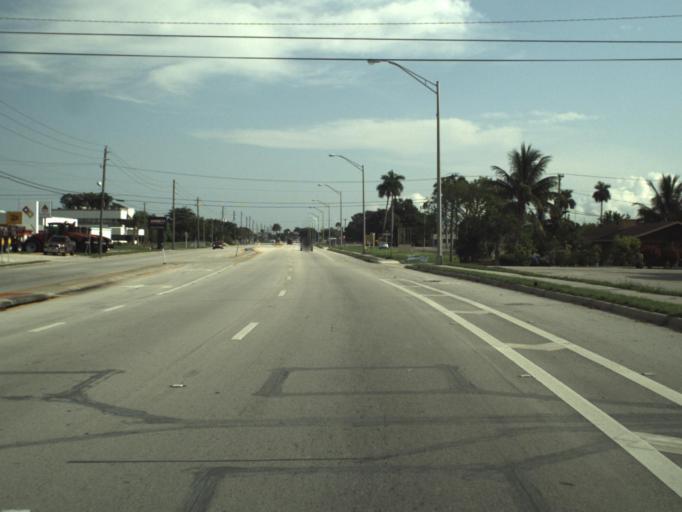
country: US
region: Florida
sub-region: Palm Beach County
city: Belle Glade Camp
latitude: 26.6674
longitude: -80.6706
